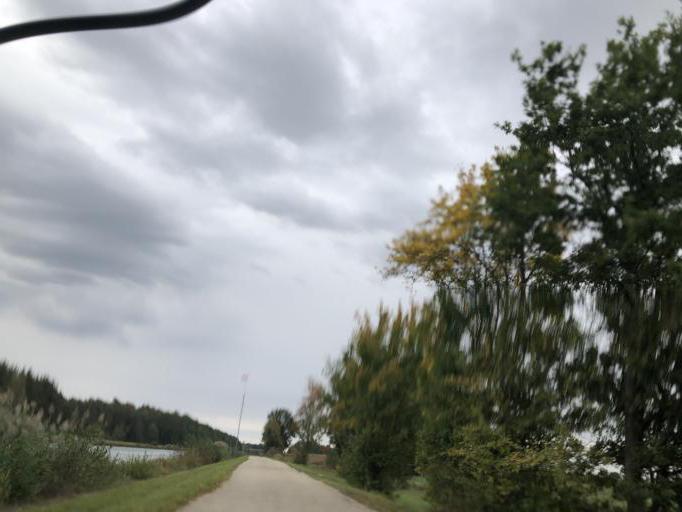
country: DE
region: Bavaria
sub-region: Regierungsbezirk Mittelfranken
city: Erlangen
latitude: 49.5505
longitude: 10.9687
